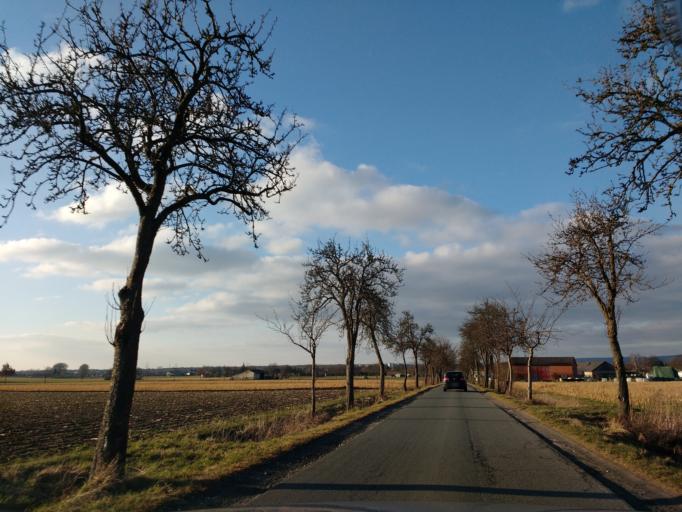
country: DE
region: North Rhine-Westphalia
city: Bad Lippspringe
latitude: 51.7653
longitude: 8.8396
